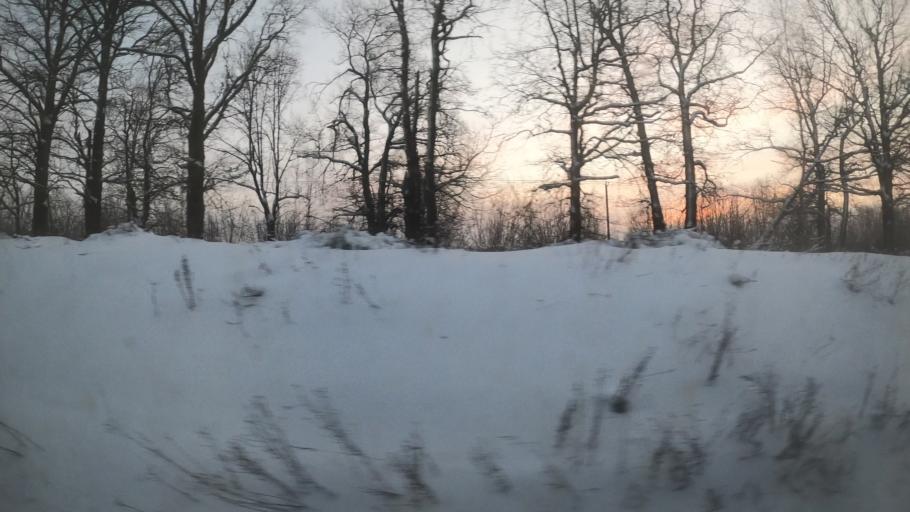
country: RU
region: Moskovskaya
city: Lugovaya
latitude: 56.0453
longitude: 37.4917
